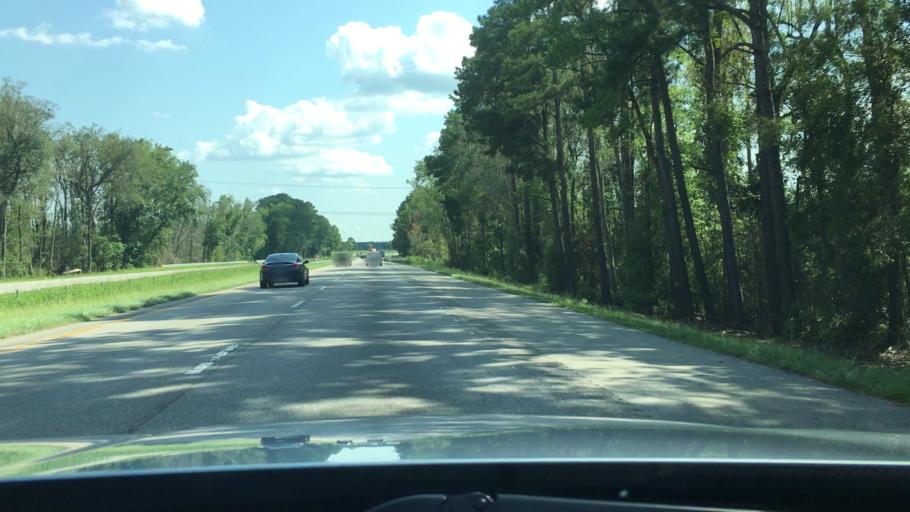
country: US
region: North Carolina
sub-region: Robeson County
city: Saint Pauls
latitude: 34.8605
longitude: -78.9655
